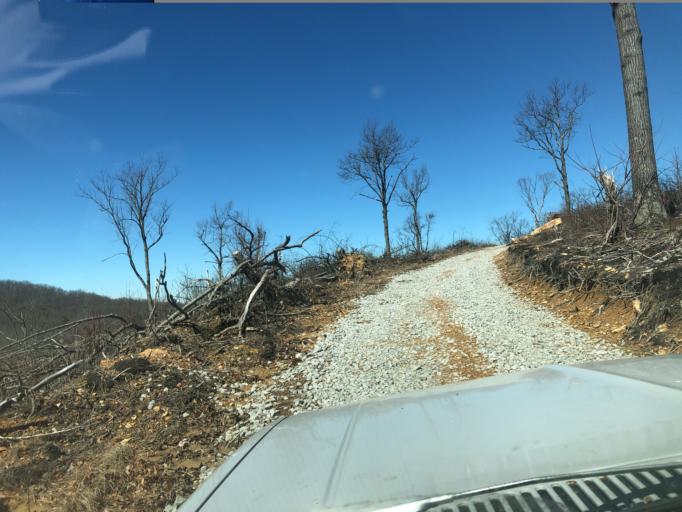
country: US
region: Tennessee
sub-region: Cumberland County
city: Fairfield Glade
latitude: 35.9712
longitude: -84.7652
